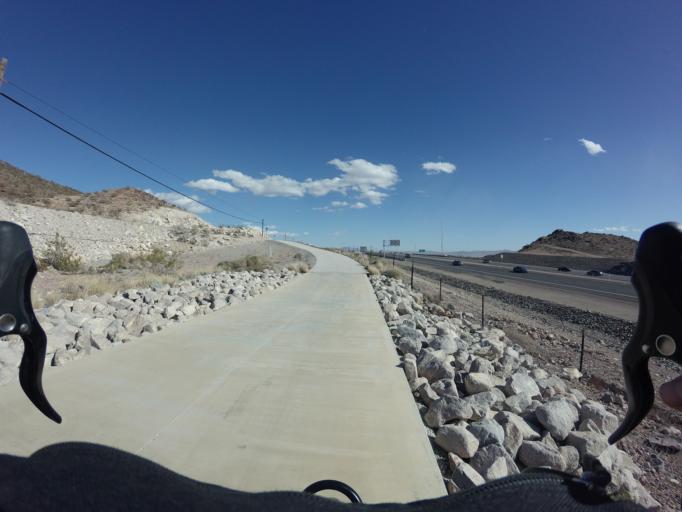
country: US
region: Nevada
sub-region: Clark County
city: Boulder City
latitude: 35.9686
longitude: -114.9037
